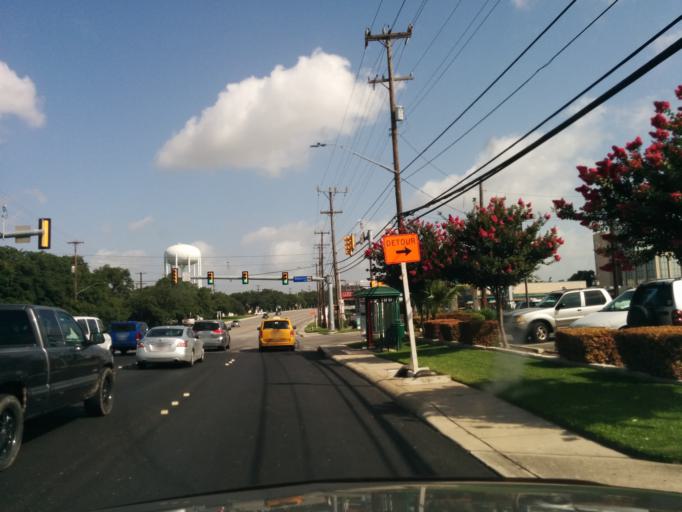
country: US
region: Texas
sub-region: Bexar County
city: Balcones Heights
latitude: 29.5139
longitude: -98.5700
